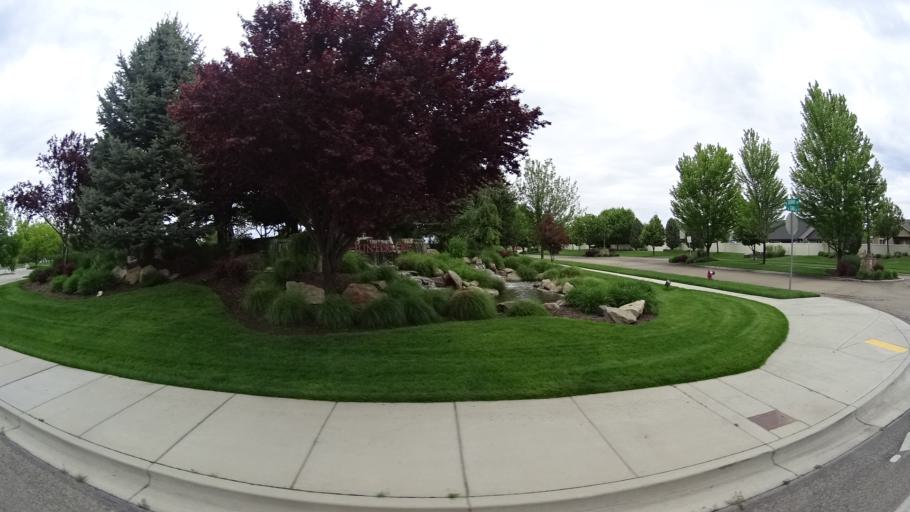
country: US
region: Idaho
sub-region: Ada County
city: Star
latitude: 43.7045
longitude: -116.4933
